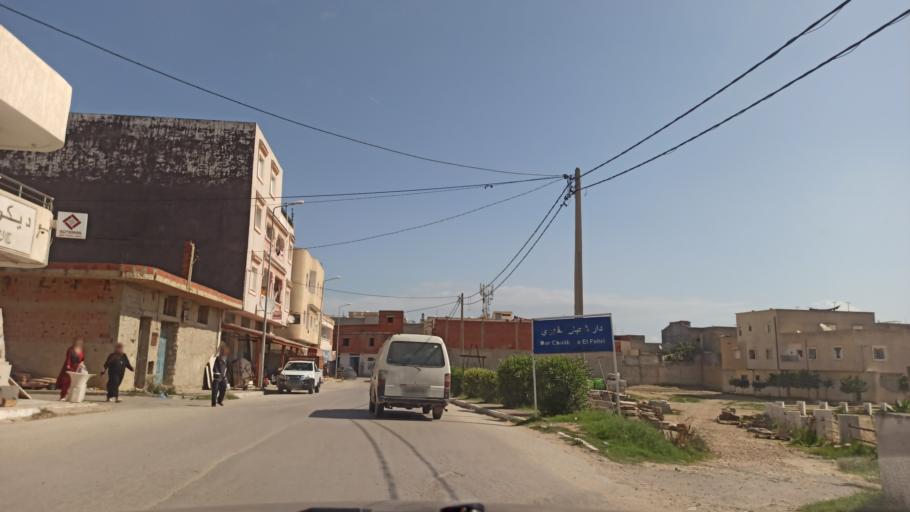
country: TN
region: Nabul
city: Nabeul
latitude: 36.4656
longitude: 10.7376
